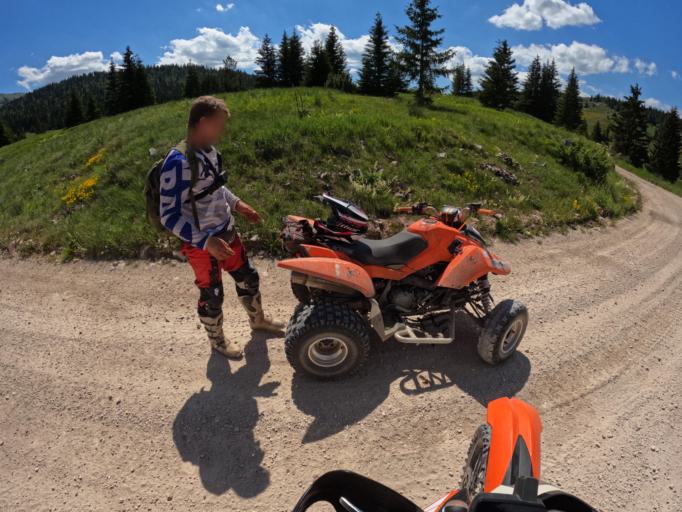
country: BA
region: Federation of Bosnia and Herzegovina
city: Livno
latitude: 43.9276
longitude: 17.0659
